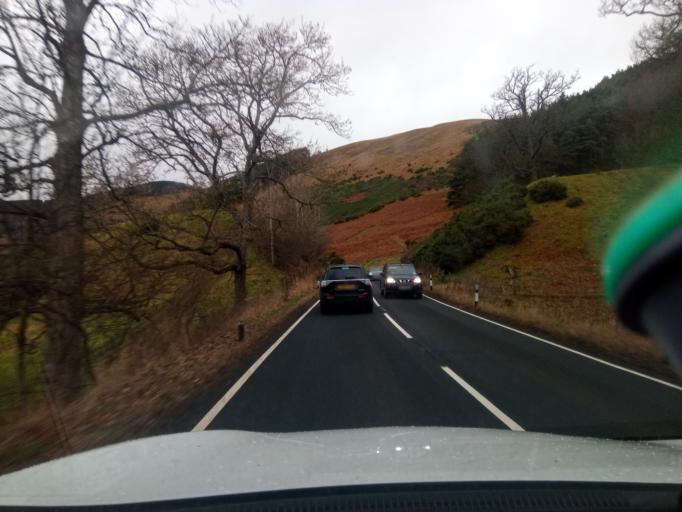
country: GB
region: Scotland
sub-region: The Scottish Borders
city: Innerleithen
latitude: 55.6283
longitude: -2.9800
